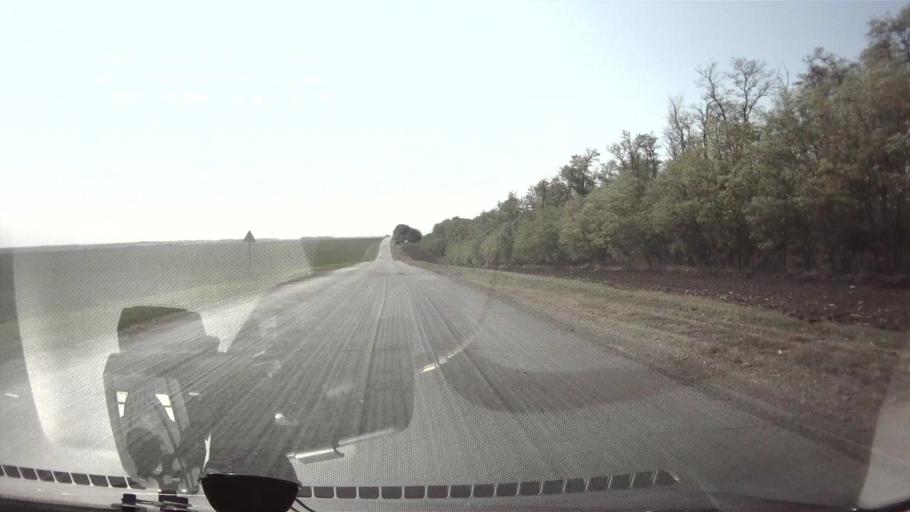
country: RU
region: Krasnodarskiy
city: Dmitriyevskaya
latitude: 45.6783
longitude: 40.7440
